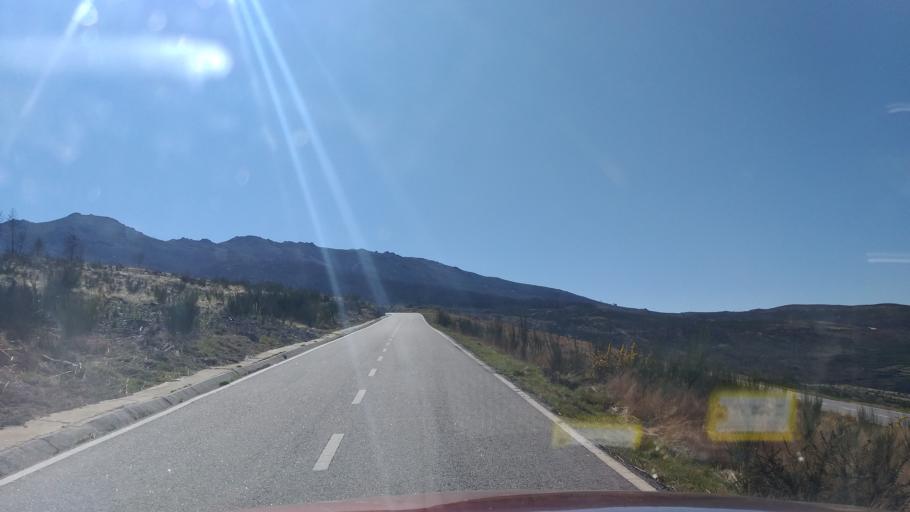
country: PT
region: Guarda
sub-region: Manteigas
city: Manteigas
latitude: 40.5011
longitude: -7.5200
